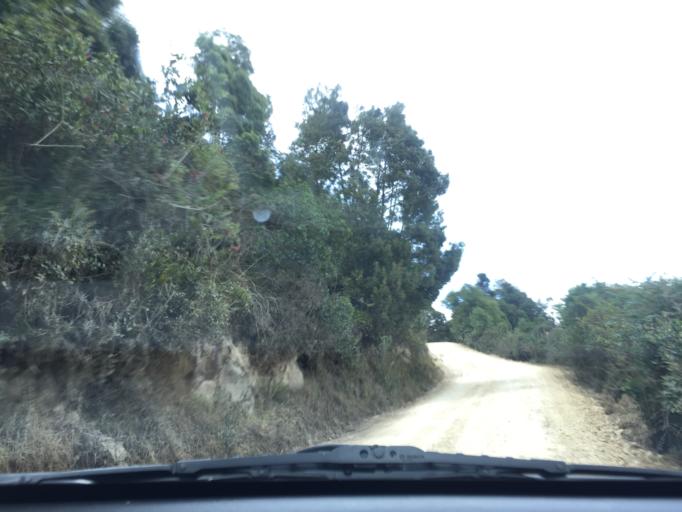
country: CO
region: Cundinamarca
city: Tabio
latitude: 4.9201
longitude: -74.1063
